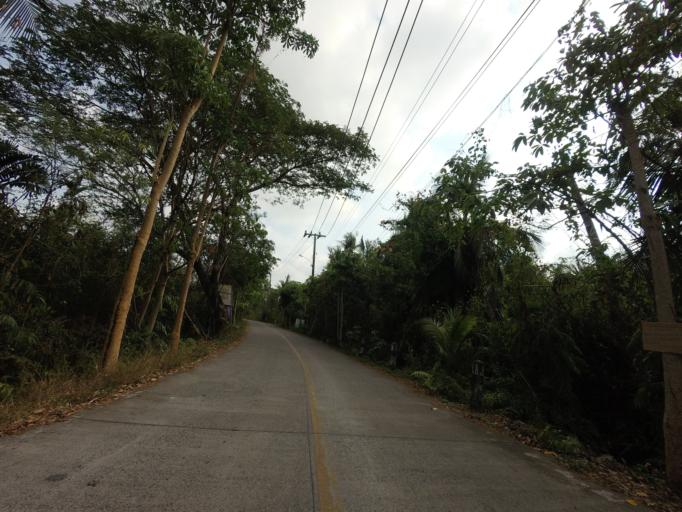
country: TH
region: Bangkok
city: Khlong Toei
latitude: 13.6981
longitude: 100.5694
